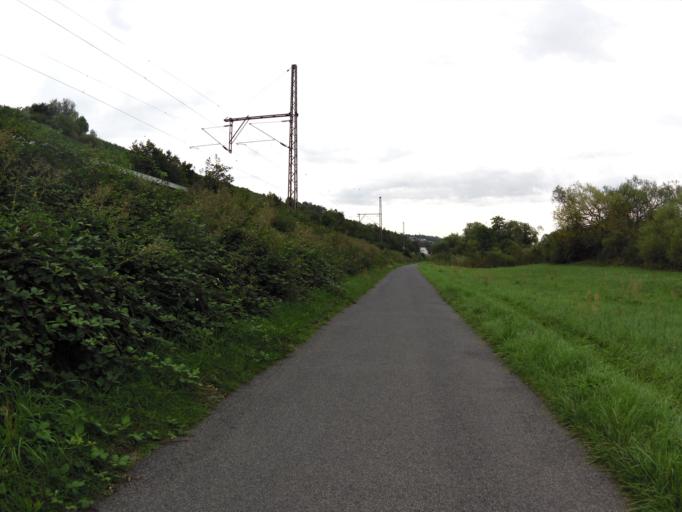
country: DE
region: Bavaria
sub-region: Regierungsbezirk Unterfranken
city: Schonungen
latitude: 50.0552
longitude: 10.2912
